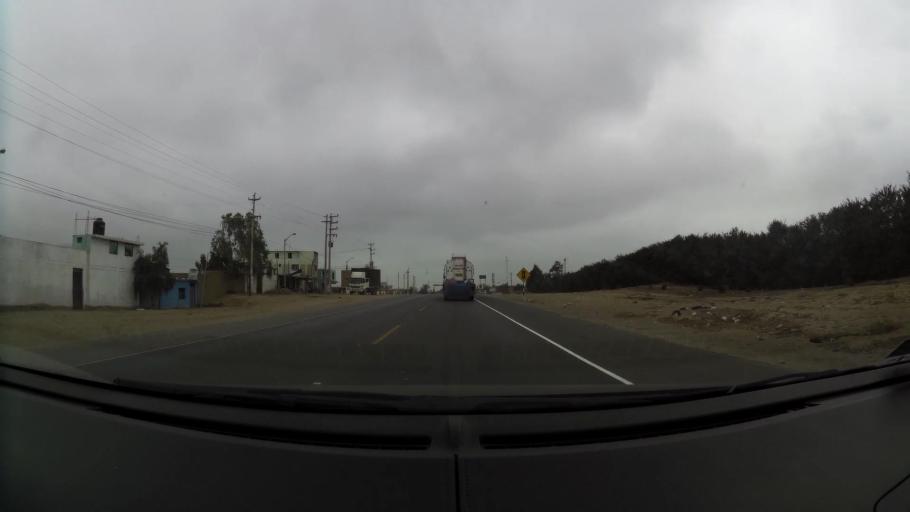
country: PE
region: La Libertad
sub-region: Viru
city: Viru
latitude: -8.4516
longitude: -78.7327
